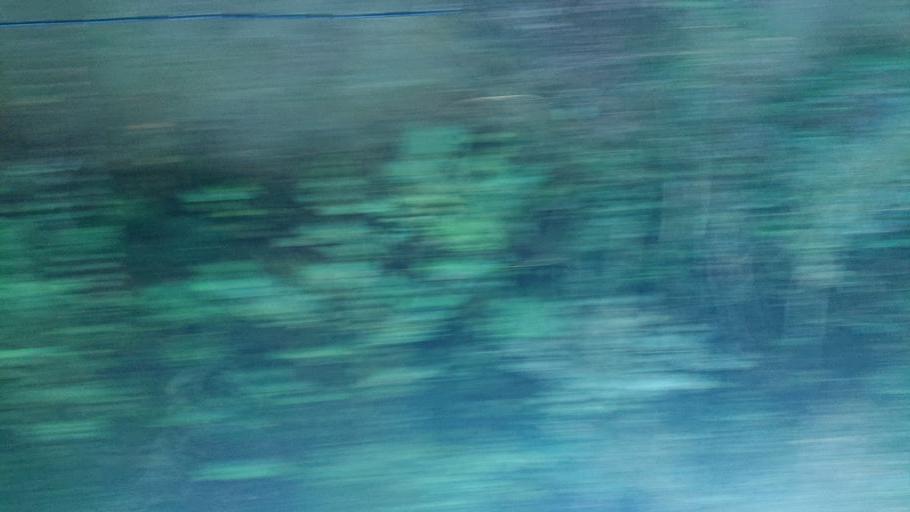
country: TW
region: Taiwan
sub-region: Yunlin
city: Douliu
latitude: 23.5309
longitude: 120.6582
